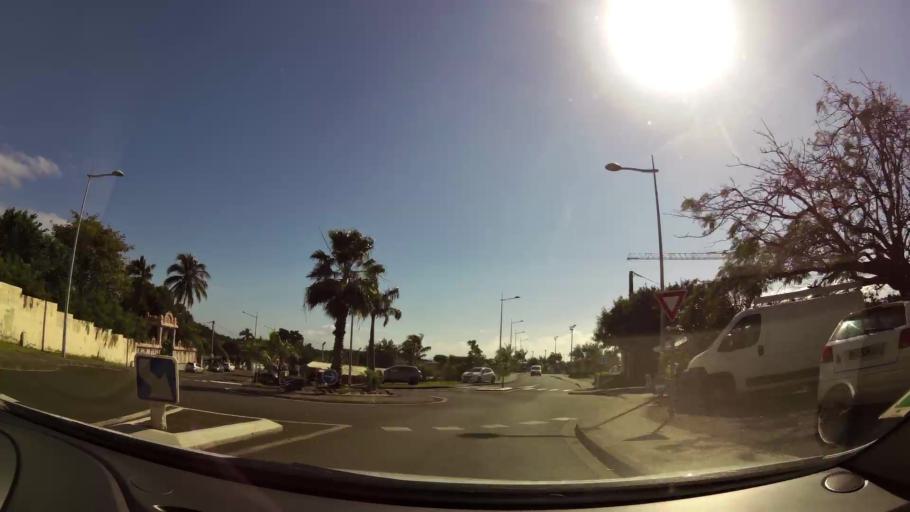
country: RE
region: Reunion
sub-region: Reunion
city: Sainte-Marie
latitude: -20.8984
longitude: 55.5019
